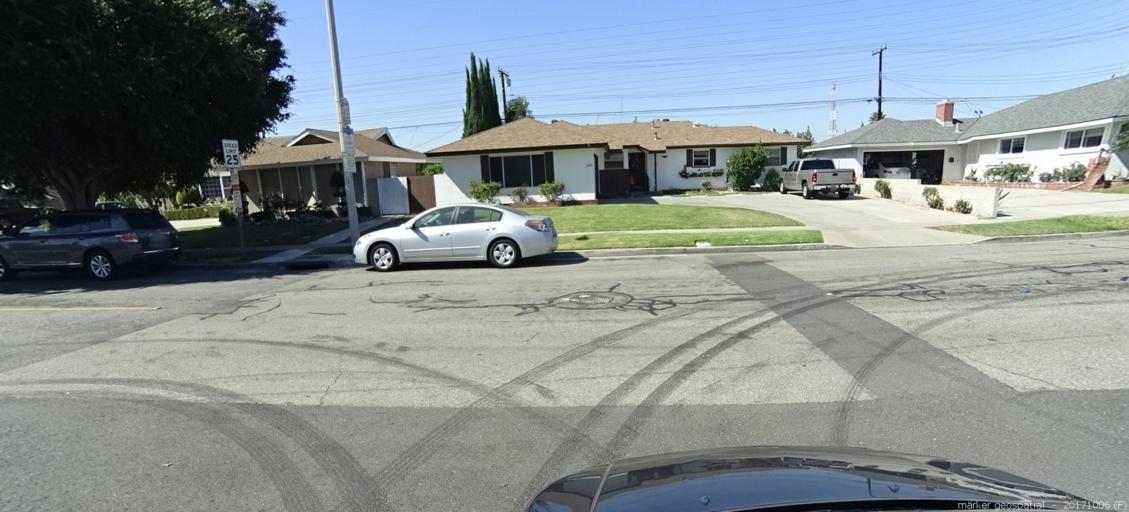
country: US
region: California
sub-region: Orange County
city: Stanton
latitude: 33.7876
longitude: -117.9982
